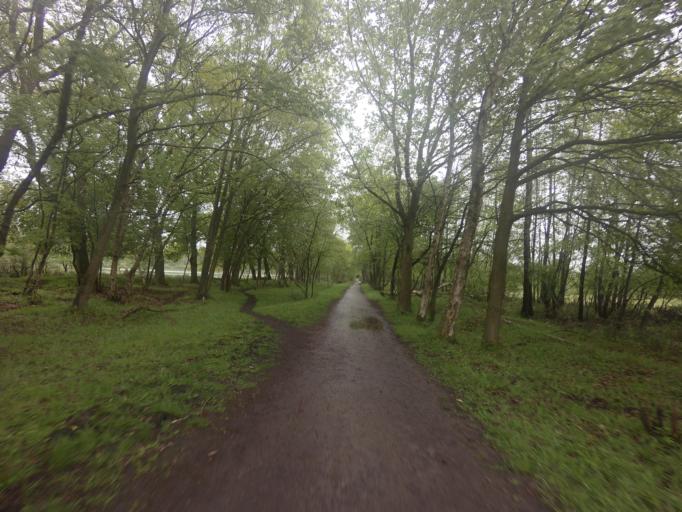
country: NL
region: Overijssel
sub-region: Gemeente Enschede
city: Enschede
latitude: 52.1443
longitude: 6.8665
